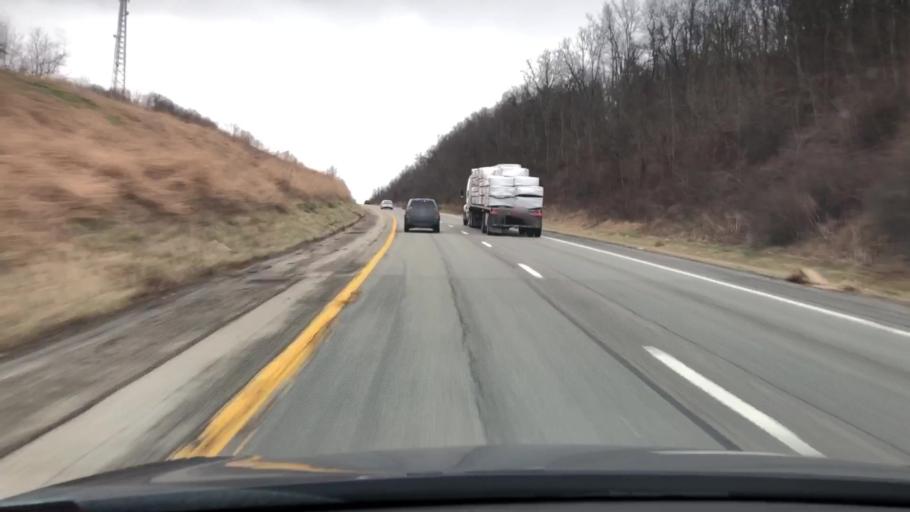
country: US
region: Pennsylvania
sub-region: Washington County
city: East Washington
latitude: 40.0797
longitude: -80.1926
